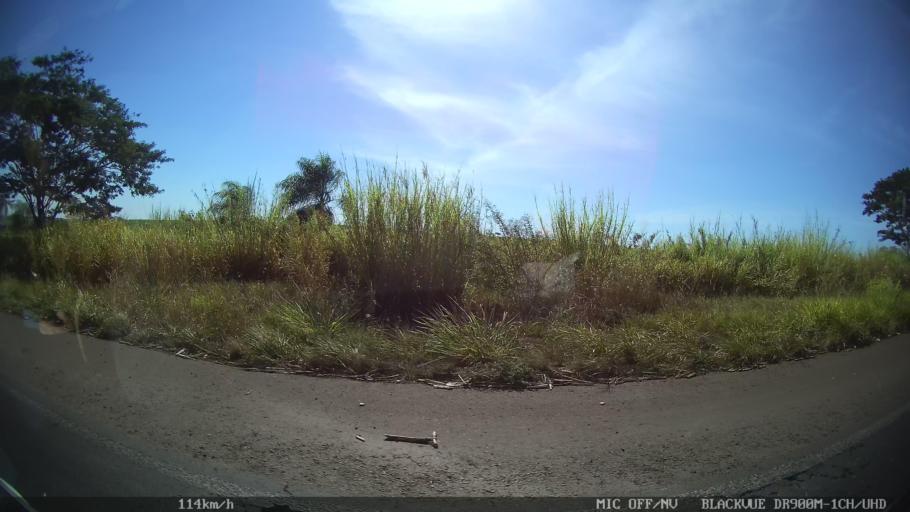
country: BR
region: Sao Paulo
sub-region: Olimpia
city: Olimpia
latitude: -20.6279
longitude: -48.7943
